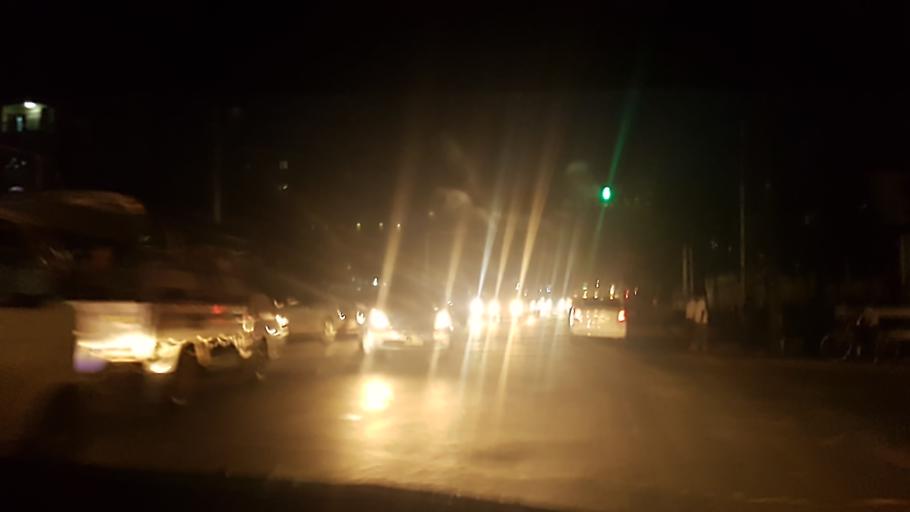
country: MM
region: Yangon
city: Yangon
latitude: 16.7837
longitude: 96.1676
